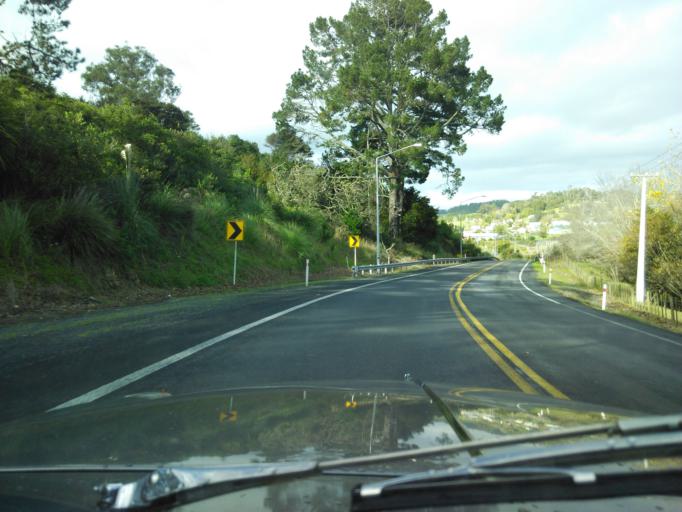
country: NZ
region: Auckland
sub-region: Auckland
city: Wellsford
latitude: -36.2503
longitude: 174.5092
